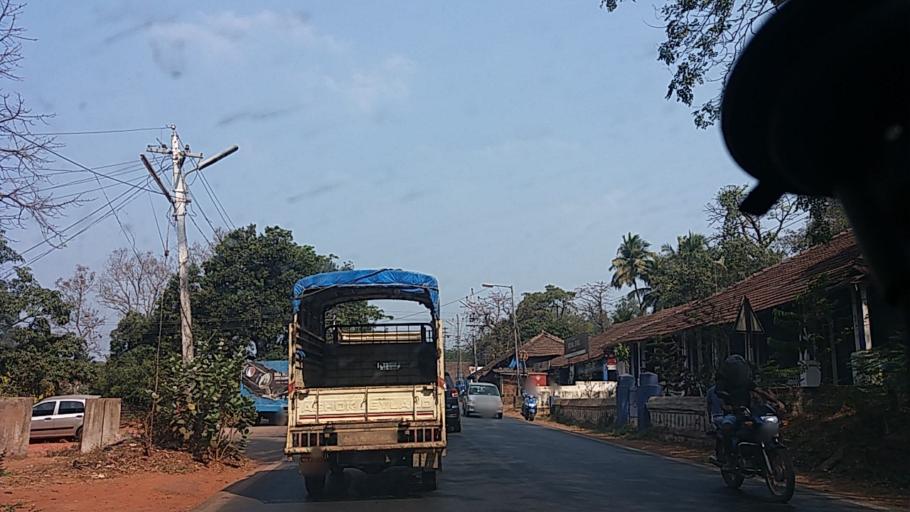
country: IN
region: Goa
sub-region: South Goa
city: Raia
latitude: 15.3071
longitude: 73.9475
